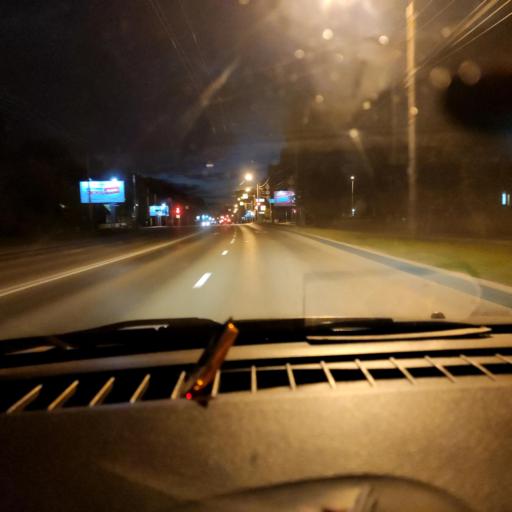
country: RU
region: Perm
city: Kondratovo
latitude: 57.9825
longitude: 56.1781
